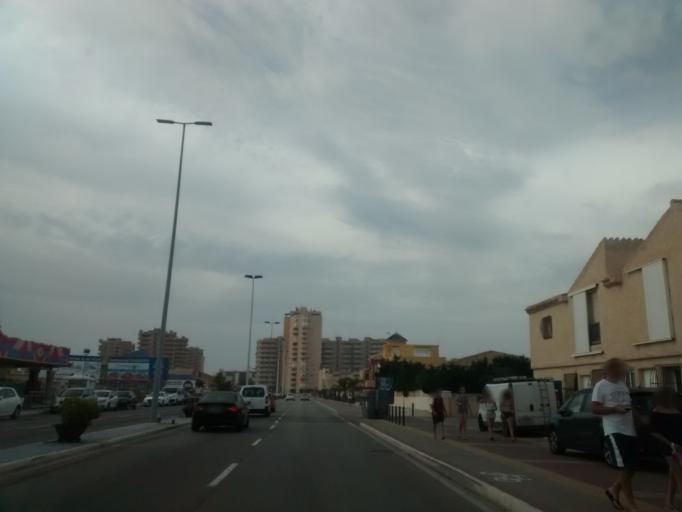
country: ES
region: Murcia
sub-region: Murcia
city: La Manga del Mar Menor
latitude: 37.6742
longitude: -0.7305
